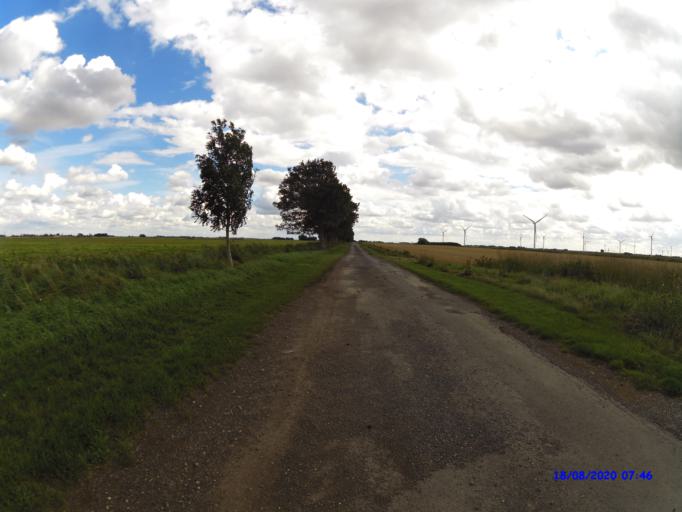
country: GB
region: England
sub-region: Cambridgeshire
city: Whittlesey
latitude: 52.5245
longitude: -0.1002
